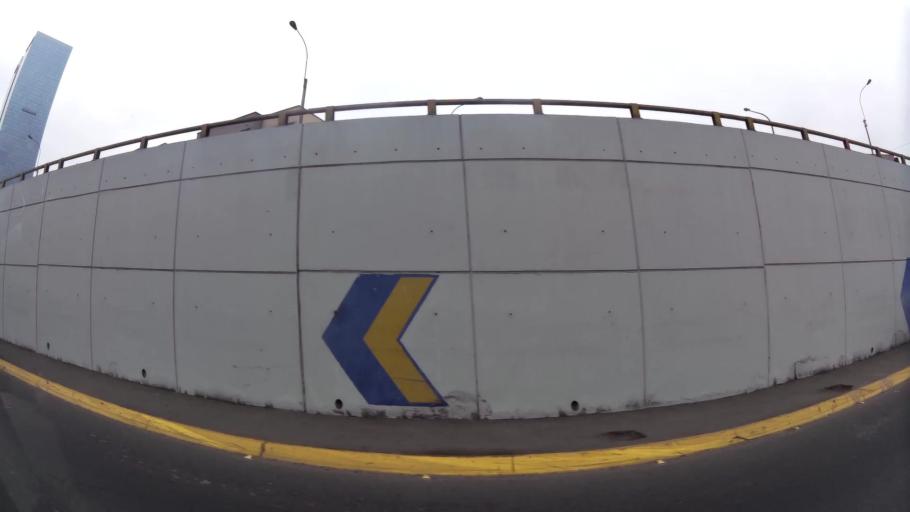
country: PE
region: Lima
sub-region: Lima
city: San Luis
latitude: -12.0871
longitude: -76.9981
